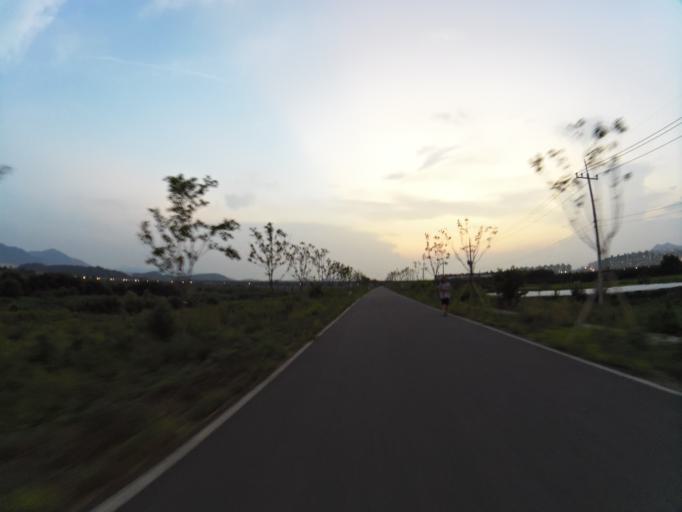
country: KR
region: Gyeongsangbuk-do
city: Gyeongsan-si
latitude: 35.8584
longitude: 128.7319
